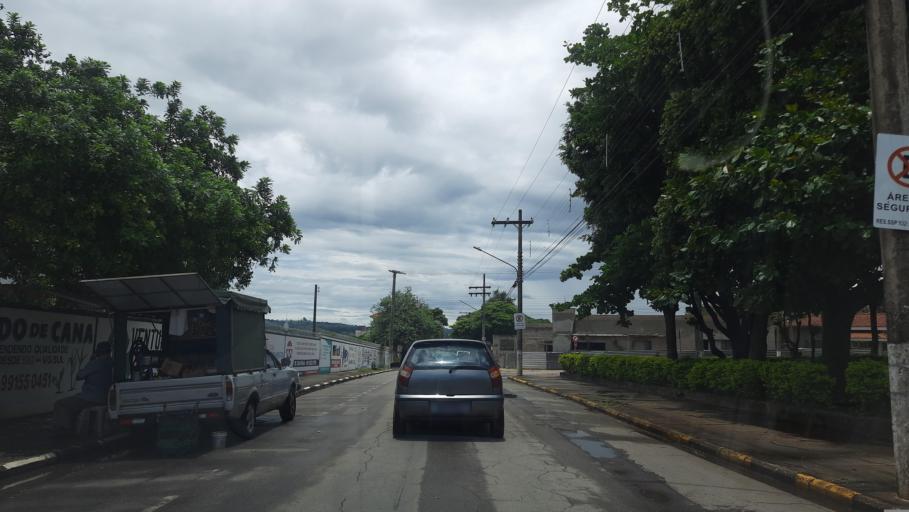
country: BR
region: Sao Paulo
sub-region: Vargem Grande Do Sul
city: Vargem Grande do Sul
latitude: -21.8394
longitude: -46.8992
